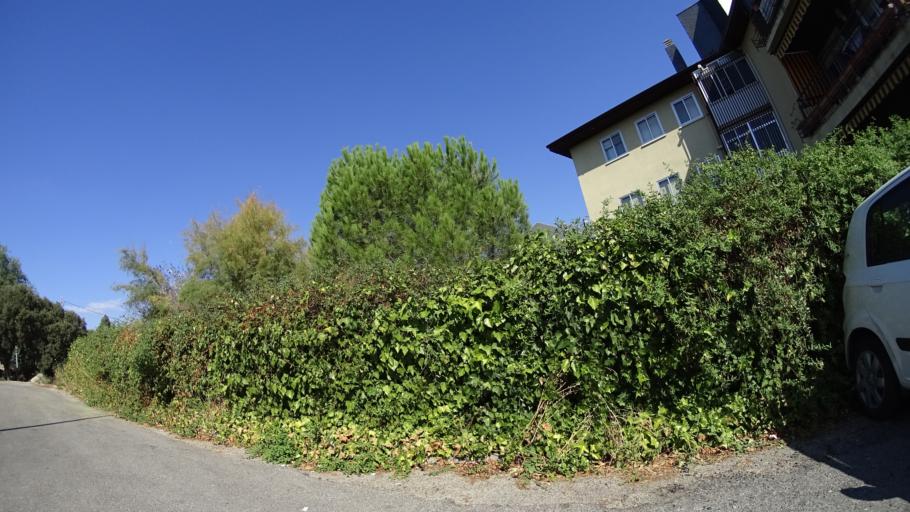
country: ES
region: Madrid
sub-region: Provincia de Madrid
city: Collado-Villalba
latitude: 40.6183
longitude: -4.0056
